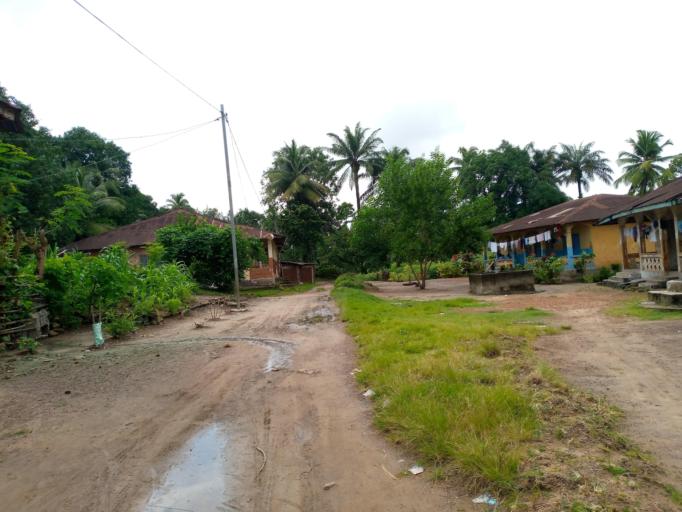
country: SL
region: Northern Province
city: Magburaka
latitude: 8.7214
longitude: -11.9467
